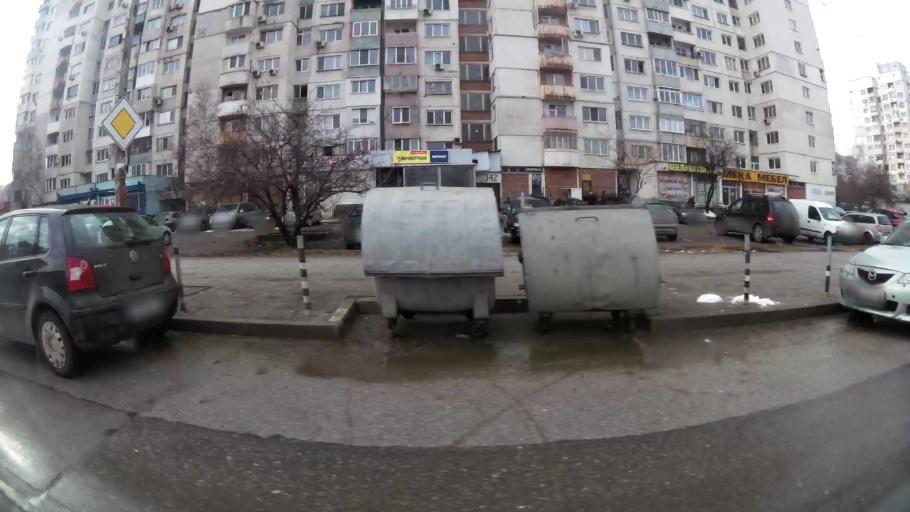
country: BG
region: Sofiya
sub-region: Obshtina Bozhurishte
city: Bozhurishte
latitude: 42.7237
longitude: 23.2475
